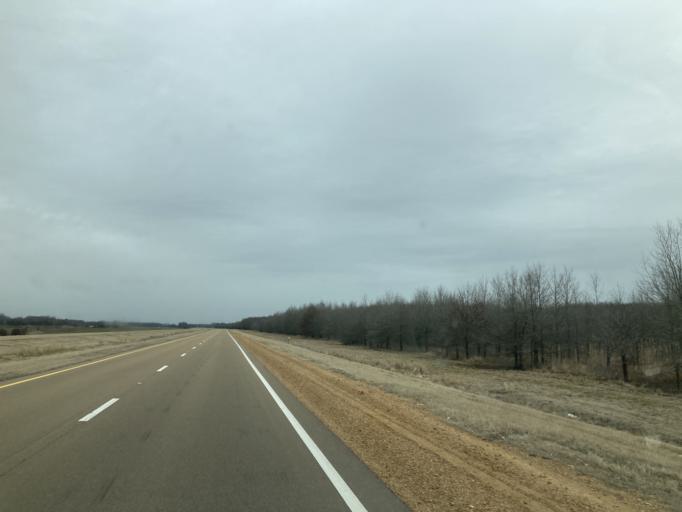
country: US
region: Mississippi
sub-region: Humphreys County
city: Belzoni
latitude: 33.0161
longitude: -90.4686
